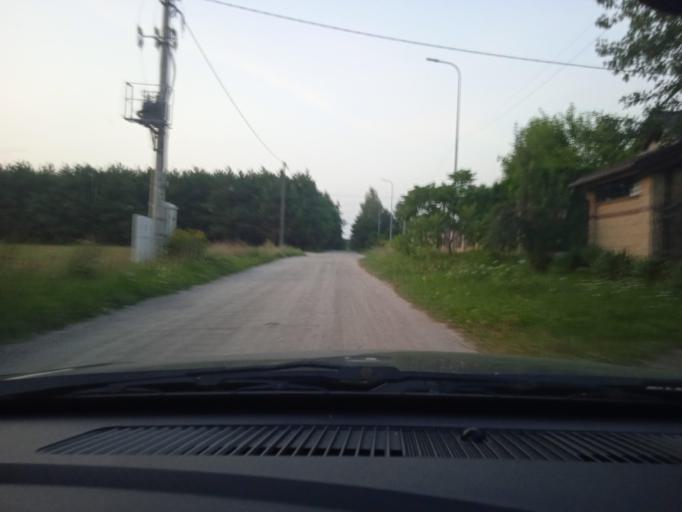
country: PL
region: Masovian Voivodeship
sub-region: Powiat nowodworski
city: Pomiechowek
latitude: 52.4876
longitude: 20.7034
